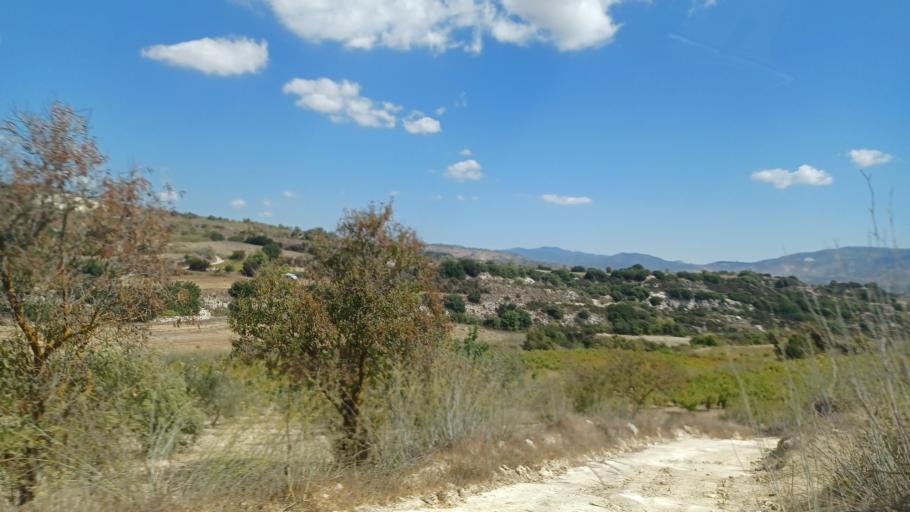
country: CY
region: Pafos
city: Mesogi
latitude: 34.8697
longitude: 32.5147
